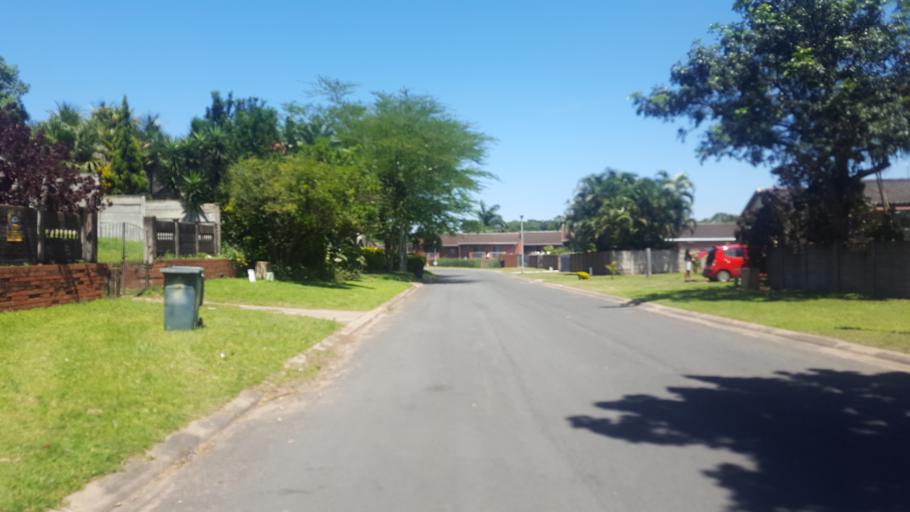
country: ZA
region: KwaZulu-Natal
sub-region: uThungulu District Municipality
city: Richards Bay
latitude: -28.7652
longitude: 32.0663
